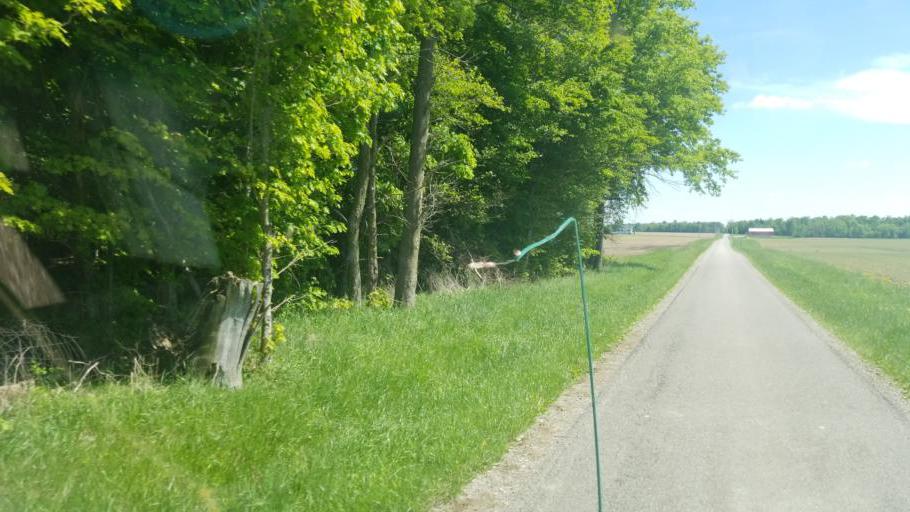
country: US
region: Ohio
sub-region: Crawford County
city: Bucyrus
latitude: 40.9421
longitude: -83.0356
